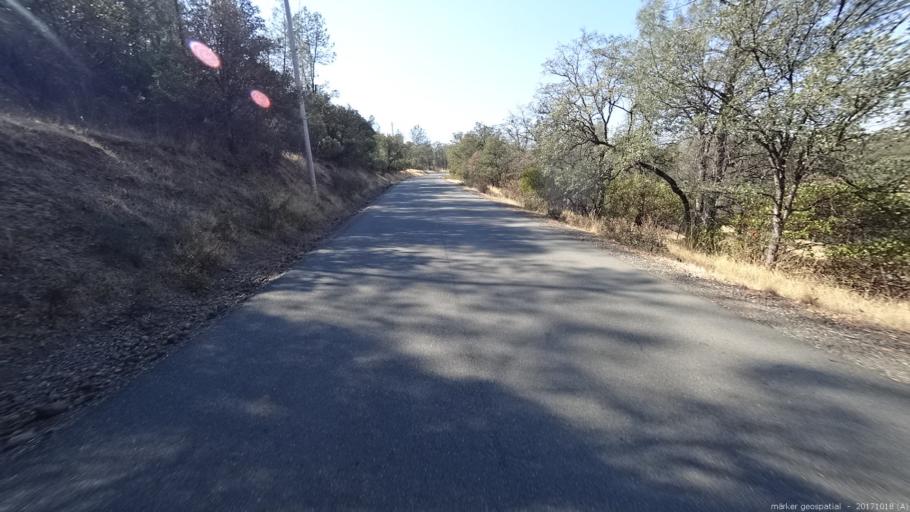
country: US
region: California
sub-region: Shasta County
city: Palo Cedro
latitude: 40.5421
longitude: -122.1075
